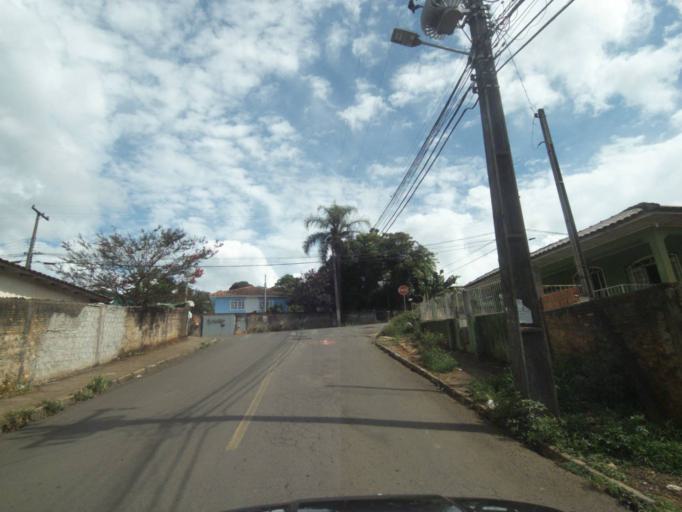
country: BR
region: Parana
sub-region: Telemaco Borba
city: Telemaco Borba
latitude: -24.3206
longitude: -50.6309
